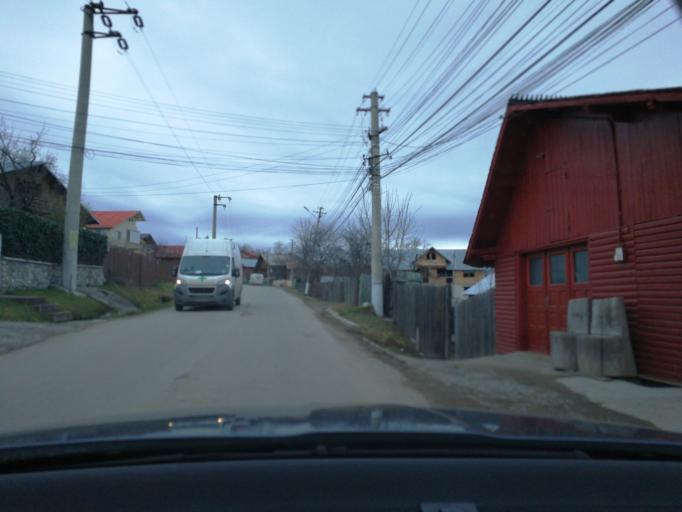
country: RO
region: Prahova
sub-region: Oras Breaza
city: Breaza
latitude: 45.1804
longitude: 25.6554
